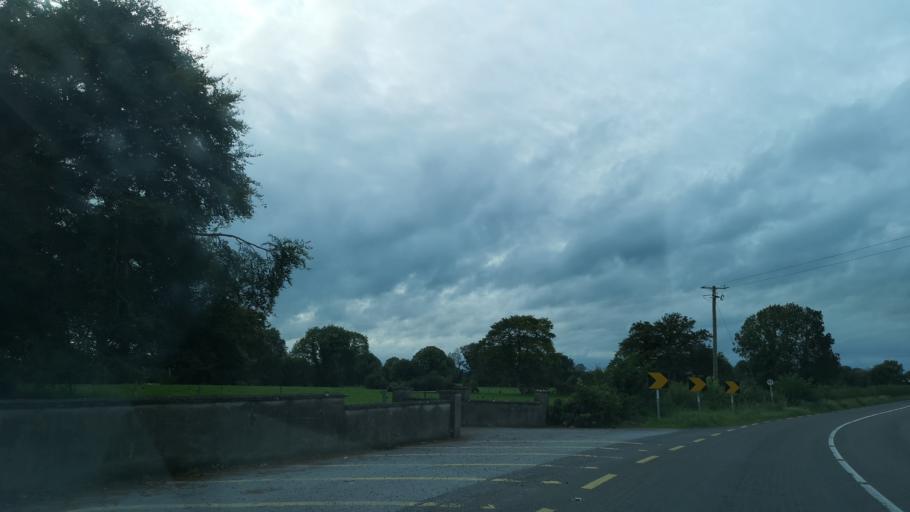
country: IE
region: Leinster
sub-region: Uibh Fhaili
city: Ferbane
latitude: 53.3618
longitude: -7.8520
